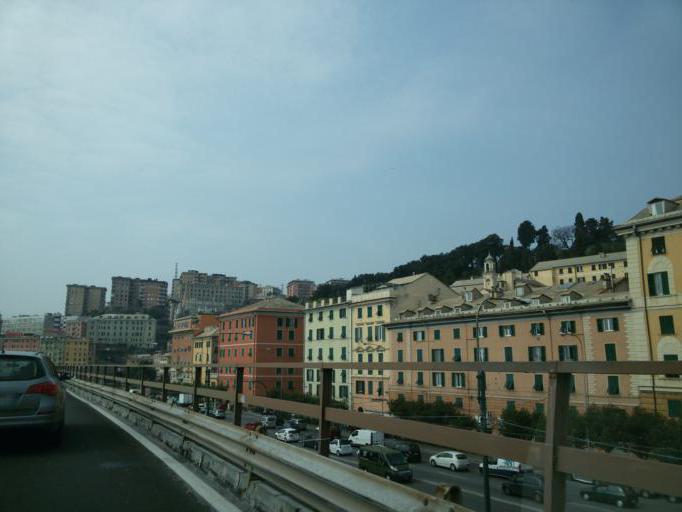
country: IT
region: Liguria
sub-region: Provincia di Genova
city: San Teodoro
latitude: 44.4144
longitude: 8.9142
